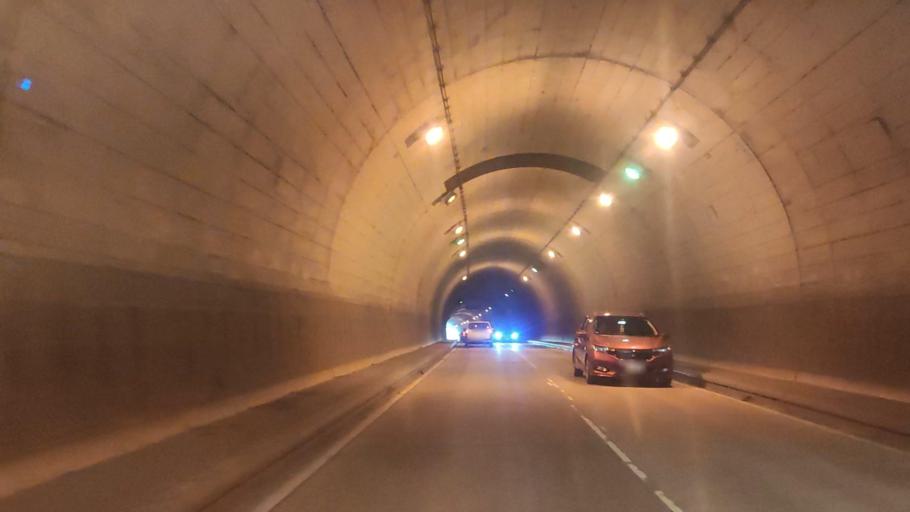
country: JP
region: Nagasaki
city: Shimabara
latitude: 32.8343
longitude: 130.2123
